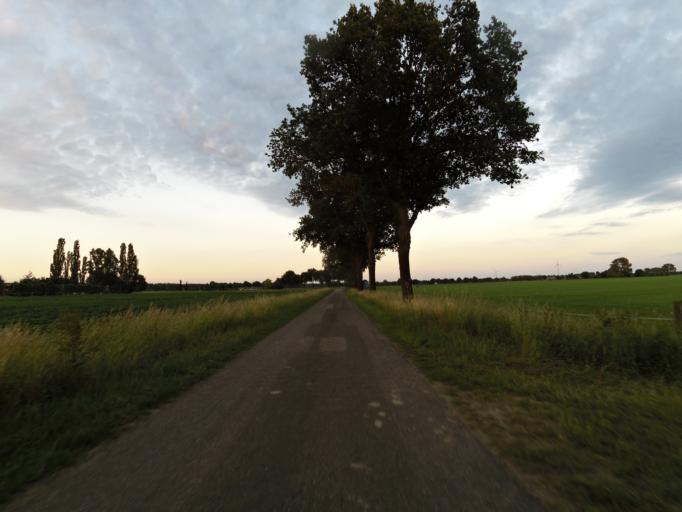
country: NL
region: Gelderland
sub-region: Oude IJsselstreek
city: Gendringen
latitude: 51.8349
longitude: 6.3924
